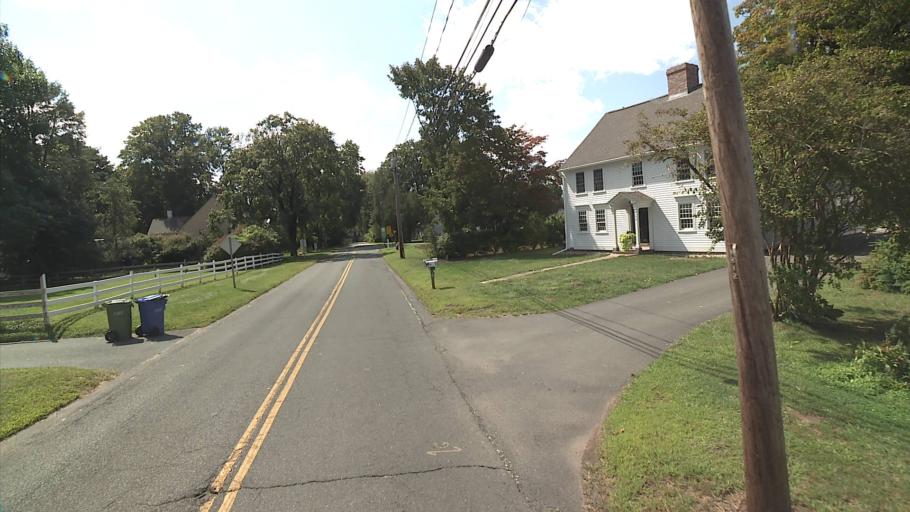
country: US
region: Connecticut
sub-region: Hartford County
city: Glastonbury Center
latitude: 41.6642
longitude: -72.6156
